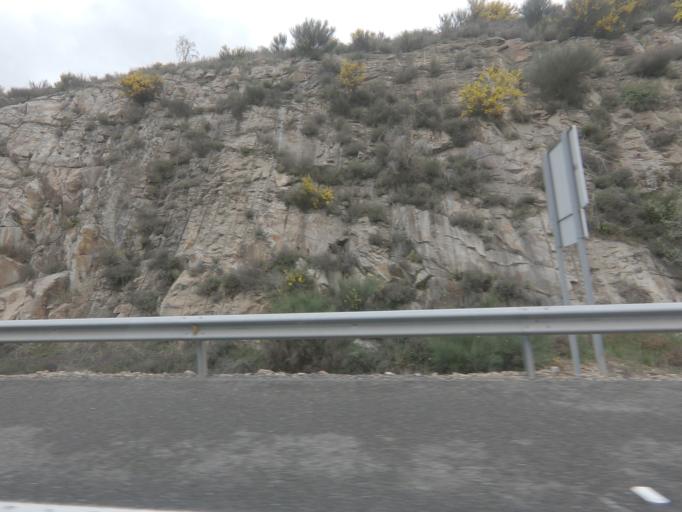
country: ES
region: Extremadura
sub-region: Provincia de Caceres
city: Aldeanueva del Camino
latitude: 40.2732
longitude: -5.9116
